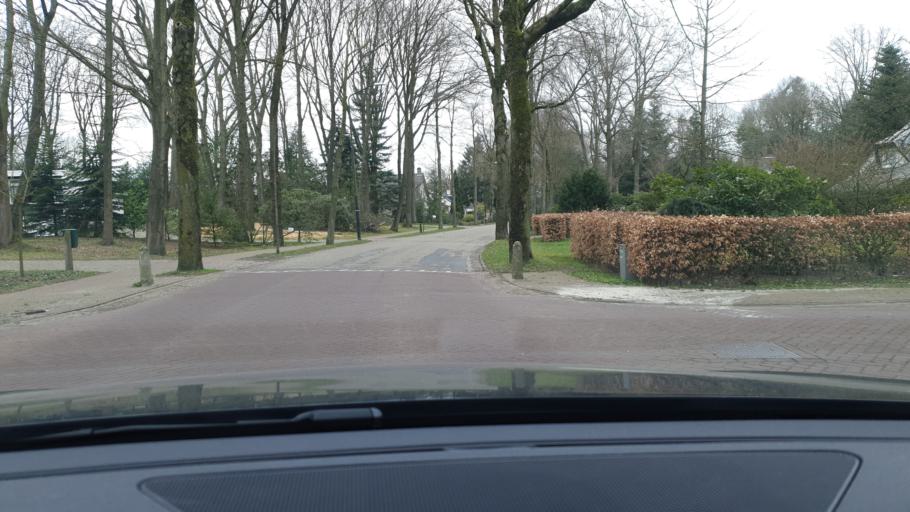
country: NL
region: North Brabant
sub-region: Gemeente Oirschot
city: Oostelbeers
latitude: 51.4174
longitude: 5.2952
